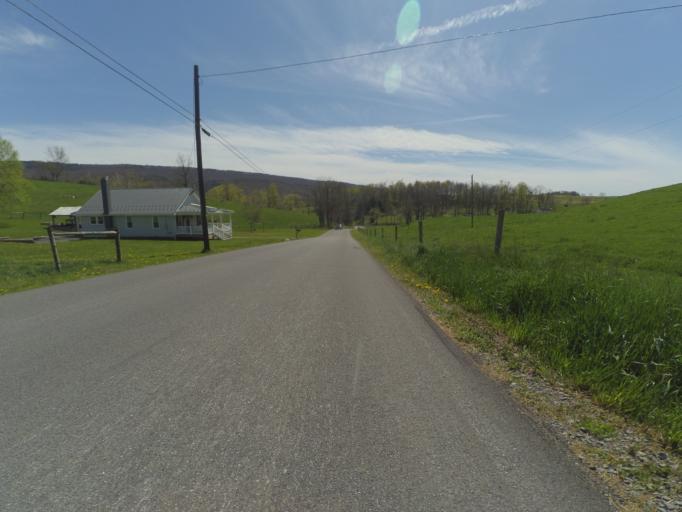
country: US
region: Pennsylvania
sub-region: Blair County
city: Tyrone
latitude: 40.6065
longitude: -78.2274
